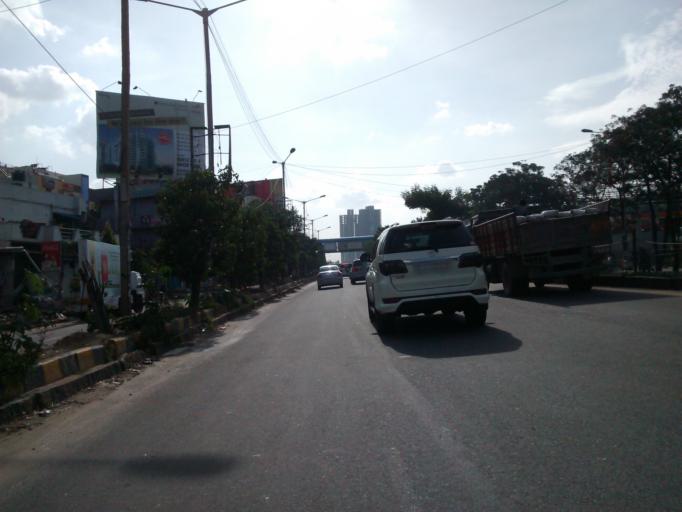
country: IN
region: Karnataka
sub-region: Bangalore Urban
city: Yelahanka
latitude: 13.0410
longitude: 77.6216
